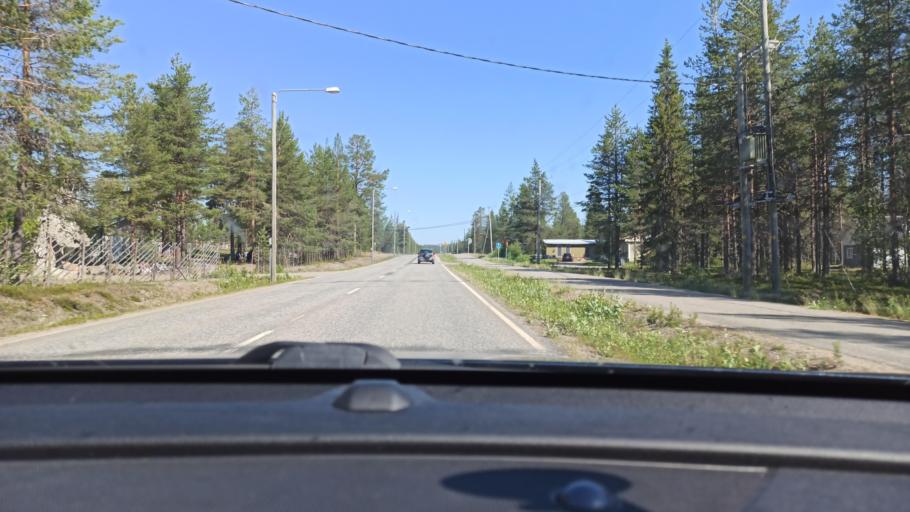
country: FI
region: Lapland
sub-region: Tunturi-Lappi
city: Kolari
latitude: 67.6215
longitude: 24.1541
